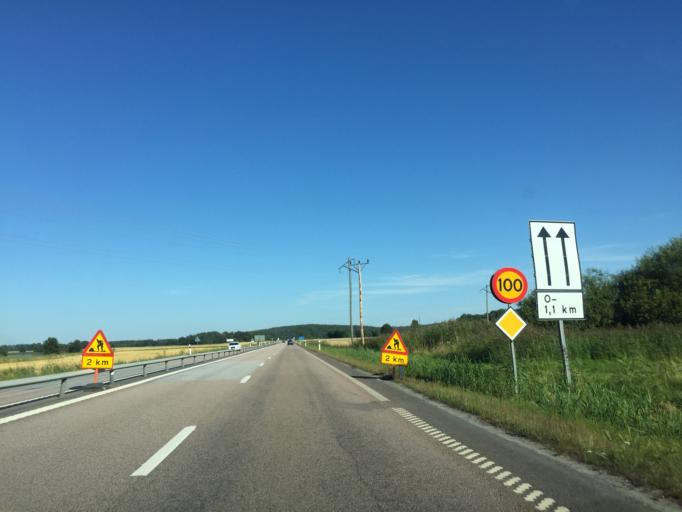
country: SE
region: Vaestmanland
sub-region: Arboga Kommun
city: Arboga
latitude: 59.3972
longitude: 15.8922
